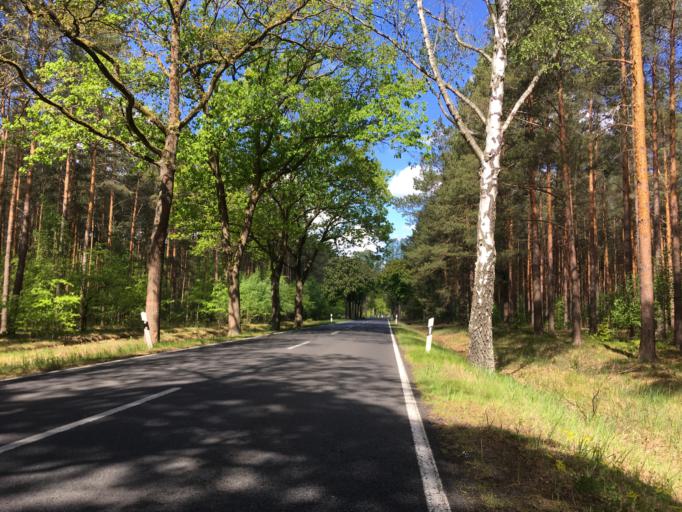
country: DE
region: Brandenburg
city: Birkenwerder
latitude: 52.7290
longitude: 13.3079
